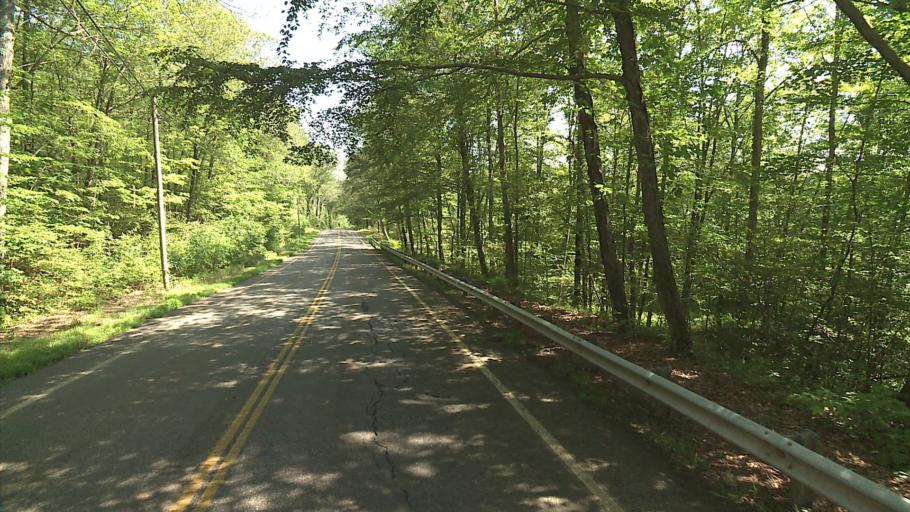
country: US
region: Connecticut
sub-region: Tolland County
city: Stafford Springs
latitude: 41.9178
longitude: -72.1820
